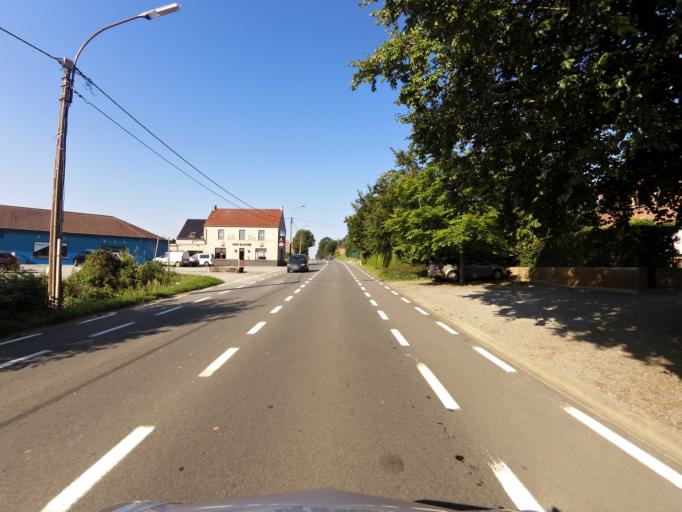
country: BE
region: Flanders
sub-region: Provincie Oost-Vlaanderen
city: Sint-Maria-Lierde
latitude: 50.8133
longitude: 3.8114
